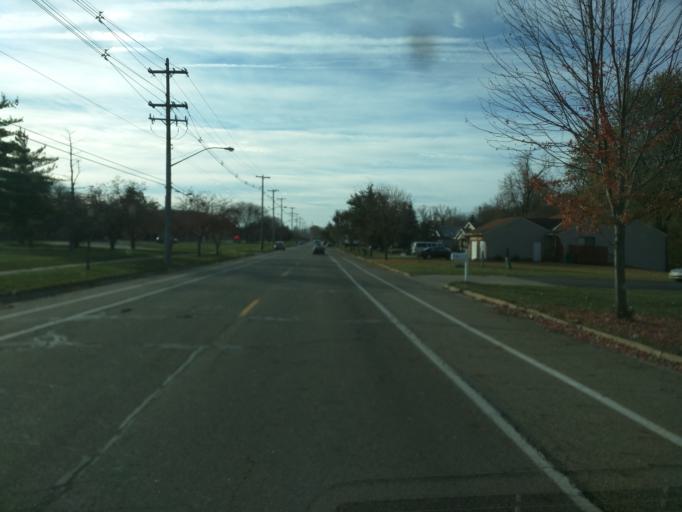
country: US
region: Michigan
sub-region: Eaton County
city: Dimondale
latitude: 42.6758
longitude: -84.5923
